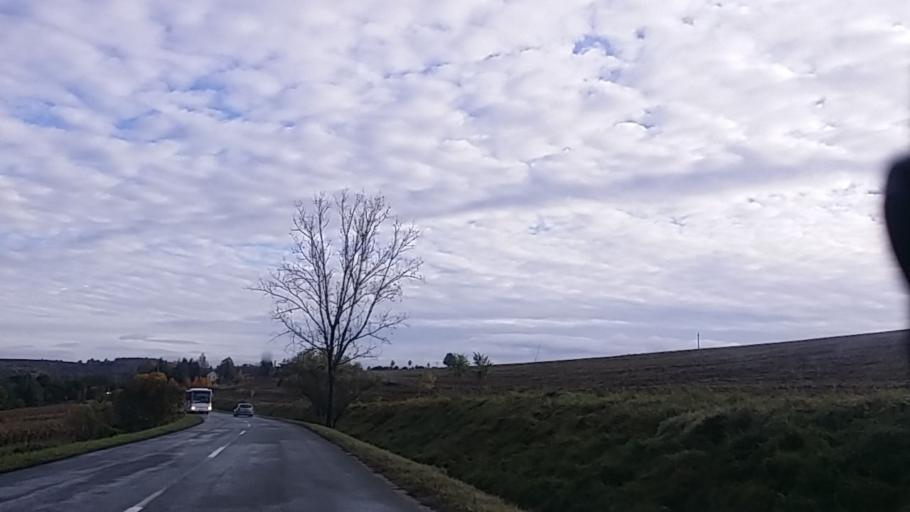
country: HU
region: Heves
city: Szilvasvarad
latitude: 48.1339
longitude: 20.4172
